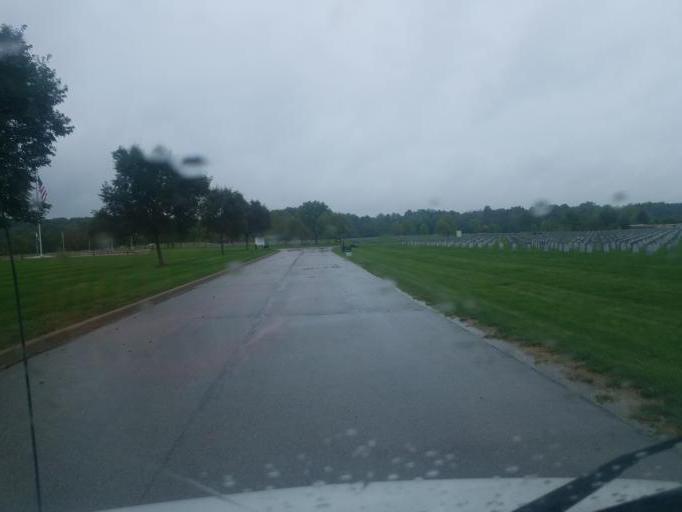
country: US
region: Ohio
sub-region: Wayne County
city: Rittman
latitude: 41.0017
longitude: -81.8107
